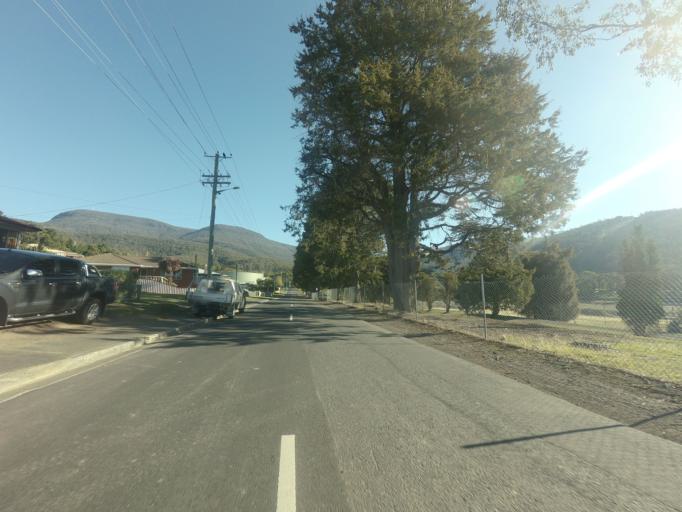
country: AU
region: Tasmania
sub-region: Glenorchy
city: West Moonah
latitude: -42.8516
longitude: 147.2553
